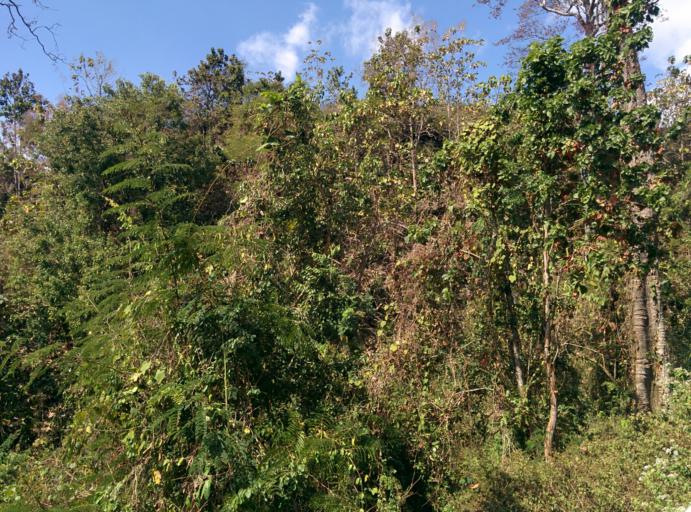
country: ID
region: East Java
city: Bacem
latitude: -8.2089
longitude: 112.2411
